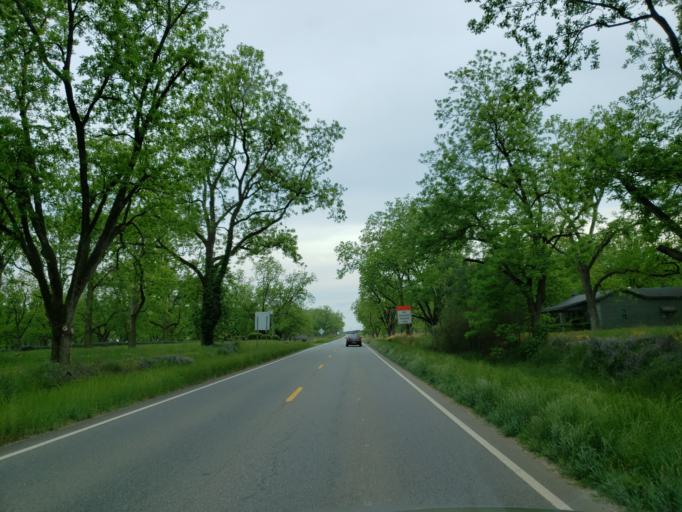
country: US
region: Georgia
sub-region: Macon County
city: Montezuma
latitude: 32.3550
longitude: -83.9677
